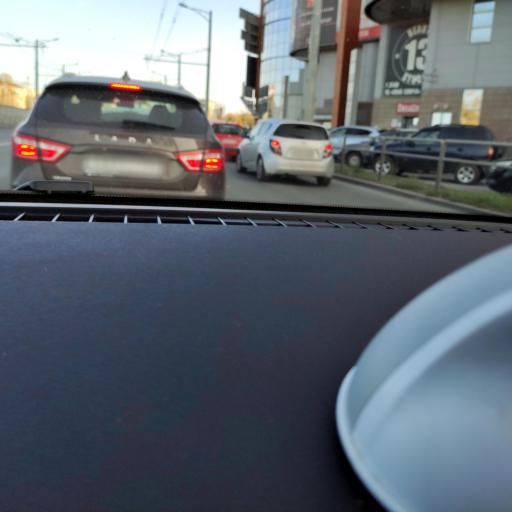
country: RU
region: Samara
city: Samara
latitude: 53.2035
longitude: 50.1558
